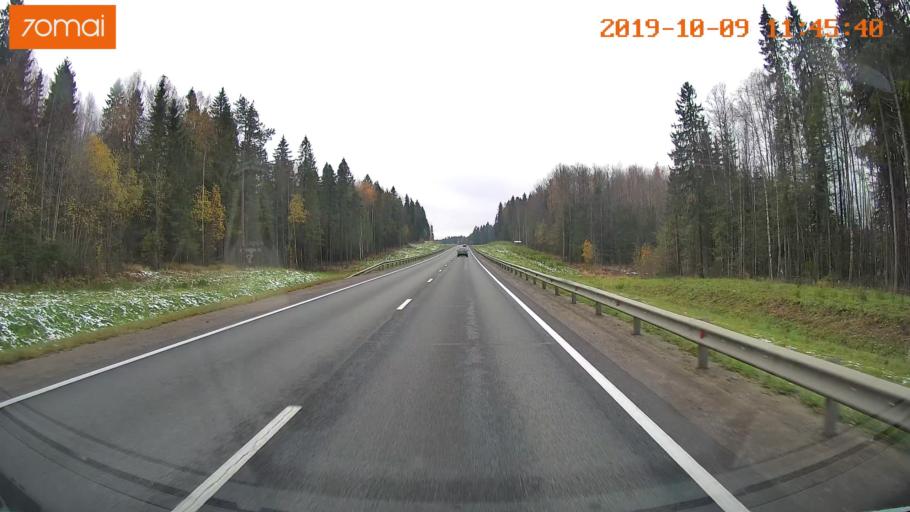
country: RU
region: Vologda
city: Gryazovets
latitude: 58.8652
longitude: 40.1980
